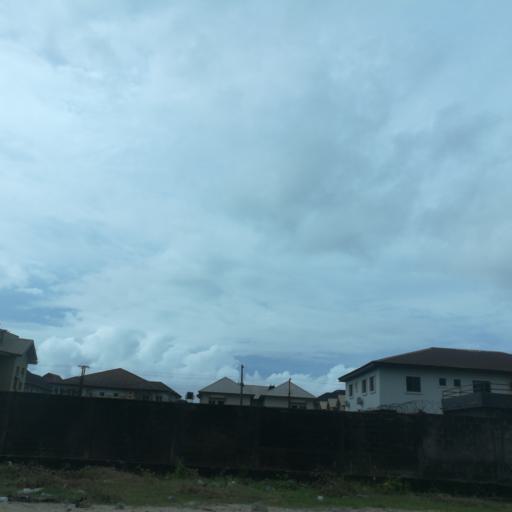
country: NG
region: Lagos
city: Ikoyi
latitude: 6.4371
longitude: 3.4700
